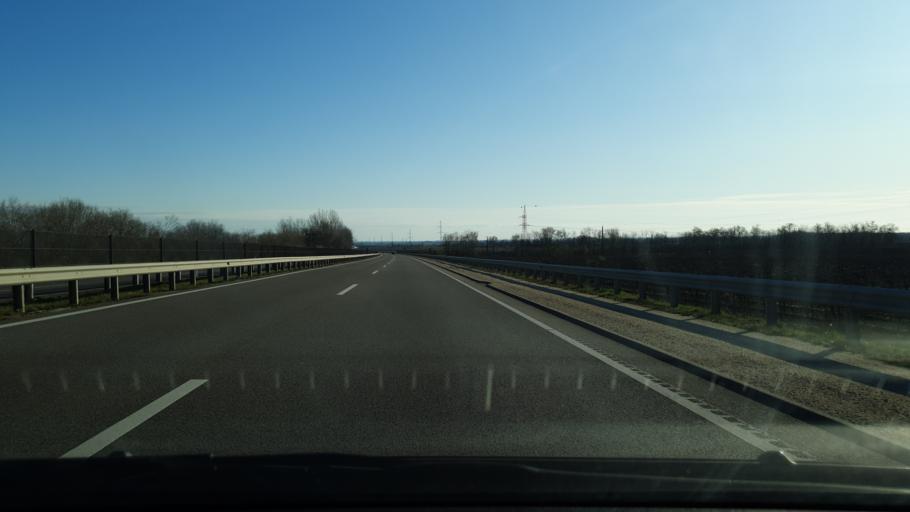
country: HU
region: Pest
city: Cegledbercel
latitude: 47.2203
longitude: 19.7001
